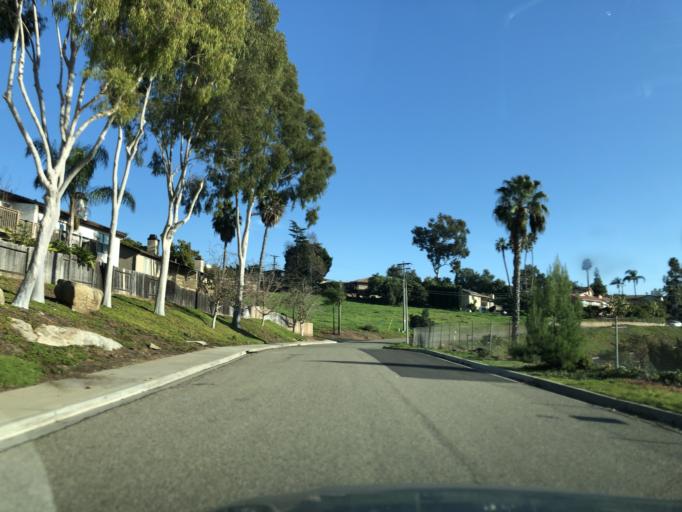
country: US
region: California
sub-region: San Diego County
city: Escondido
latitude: 33.1360
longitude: -117.0990
